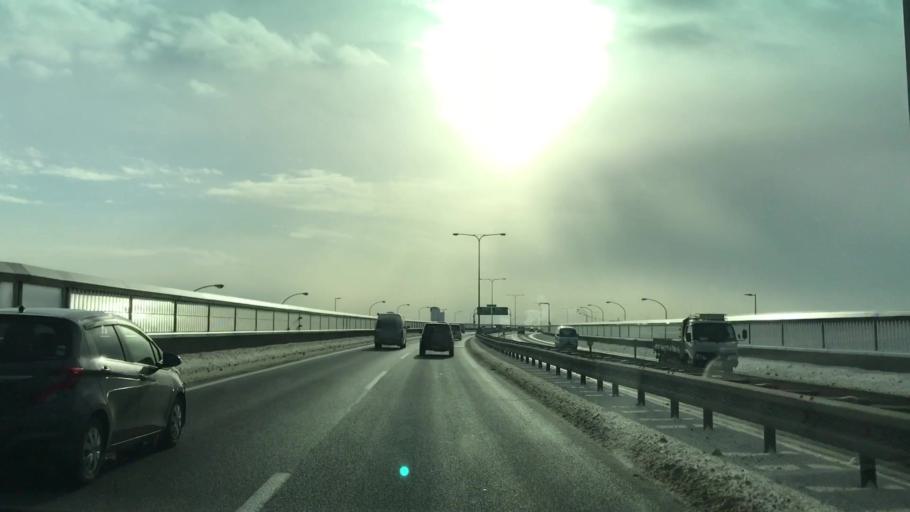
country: JP
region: Hokkaido
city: Sapporo
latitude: 43.0867
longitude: 141.4164
